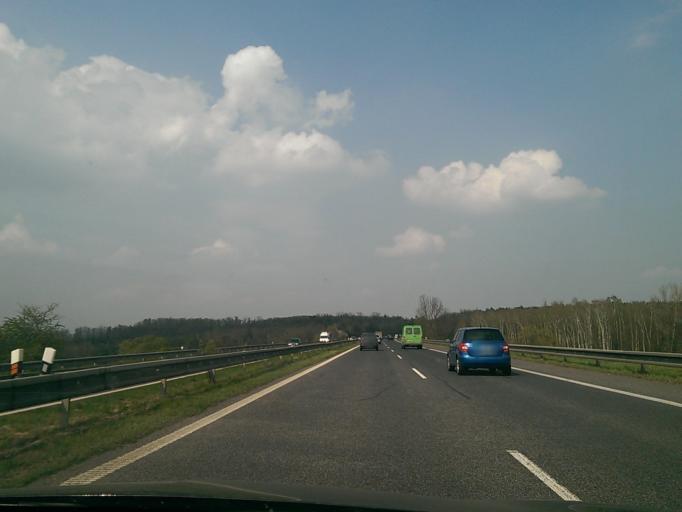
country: CZ
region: Central Bohemia
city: Benatky nad Jizerou
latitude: 50.3067
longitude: 14.8586
